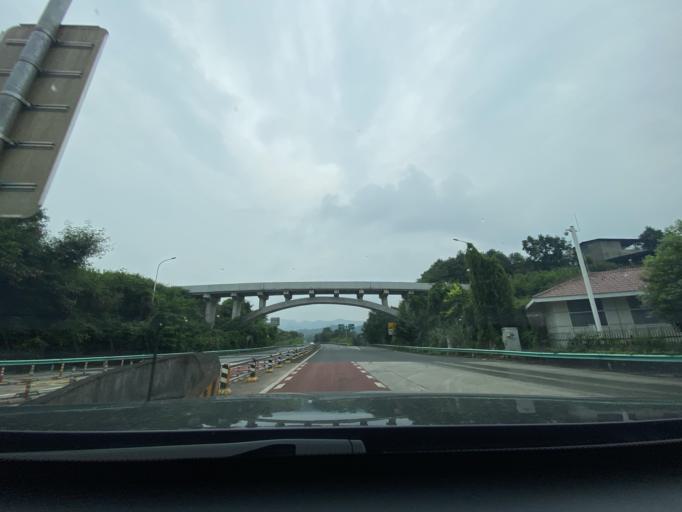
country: CN
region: Sichuan
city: Wenlin
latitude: 30.2948
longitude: 104.1210
